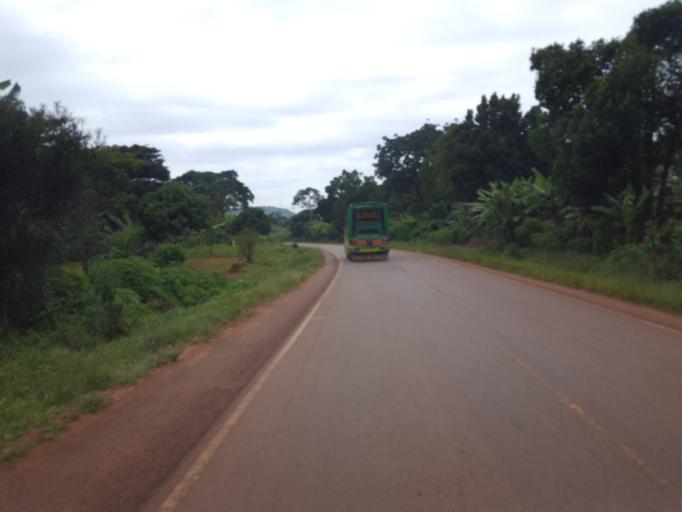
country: UG
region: Central Region
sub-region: Mityana District
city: Mityana
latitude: 0.6661
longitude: 32.0879
